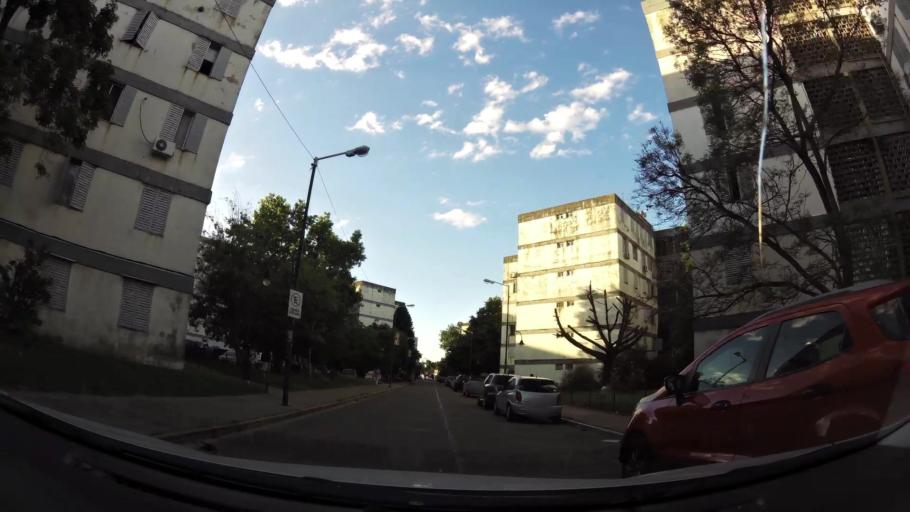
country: AR
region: Buenos Aires
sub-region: Partido de Tigre
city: Tigre
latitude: -34.4477
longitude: -58.5749
